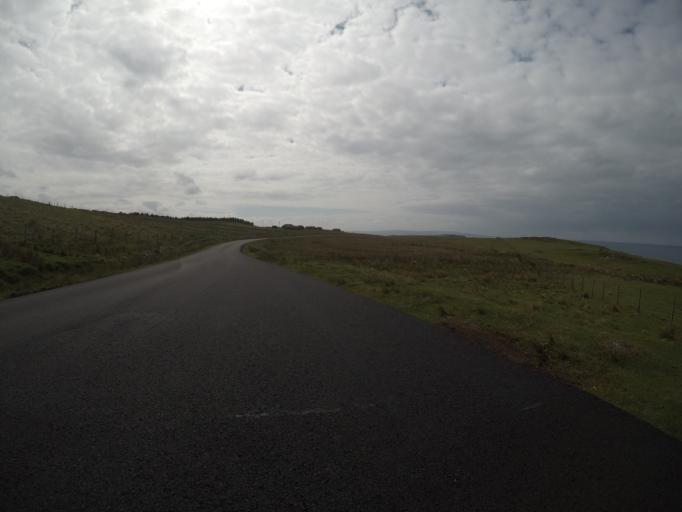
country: GB
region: Scotland
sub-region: Highland
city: Portree
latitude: 57.6627
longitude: -6.3661
